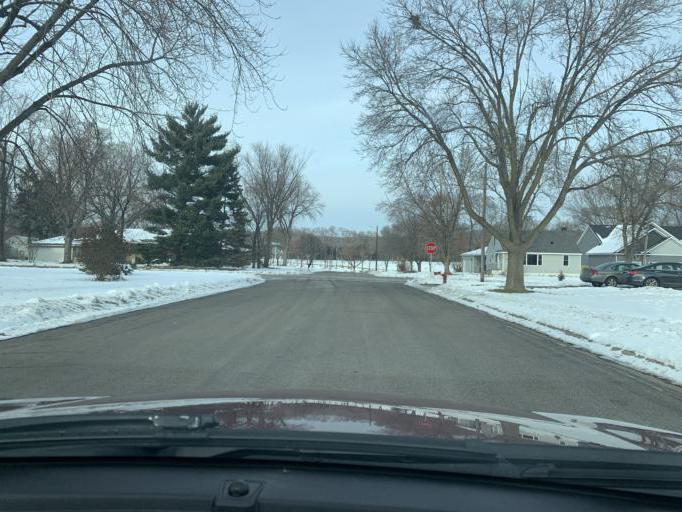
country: US
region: Minnesota
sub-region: Washington County
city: Saint Paul Park
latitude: 44.8400
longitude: -92.9813
